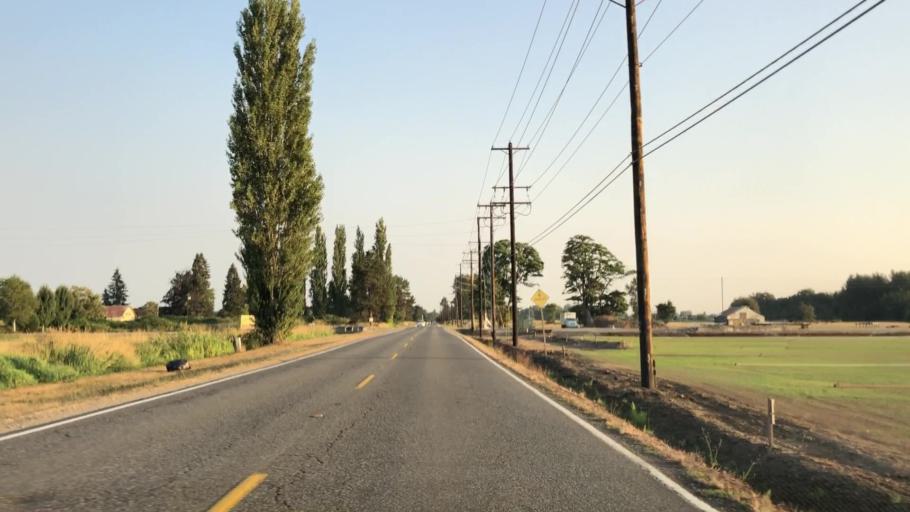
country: US
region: Washington
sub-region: Snohomish County
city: Smokey Point
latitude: 48.1444
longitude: -122.1617
